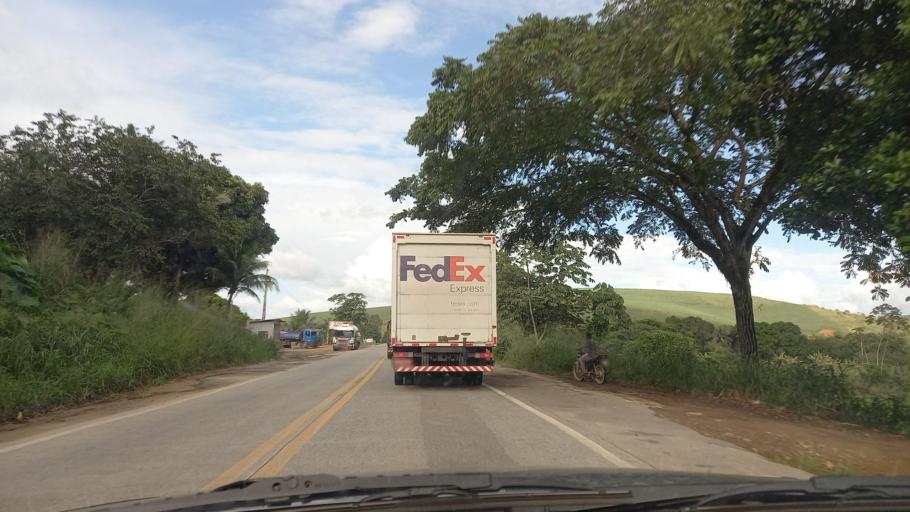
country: BR
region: Pernambuco
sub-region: Catende
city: Catende
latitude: -8.6958
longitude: -35.6640
